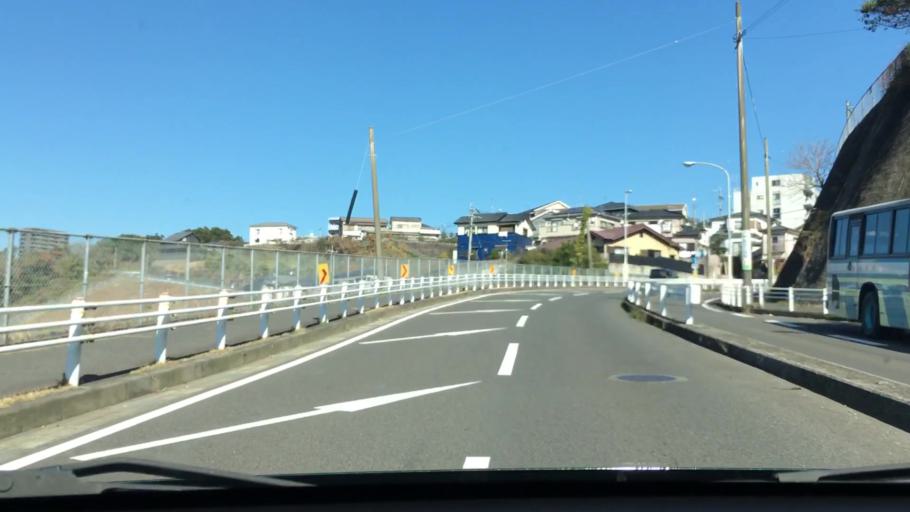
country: JP
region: Kagoshima
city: Kagoshima-shi
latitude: 31.5586
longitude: 130.5263
